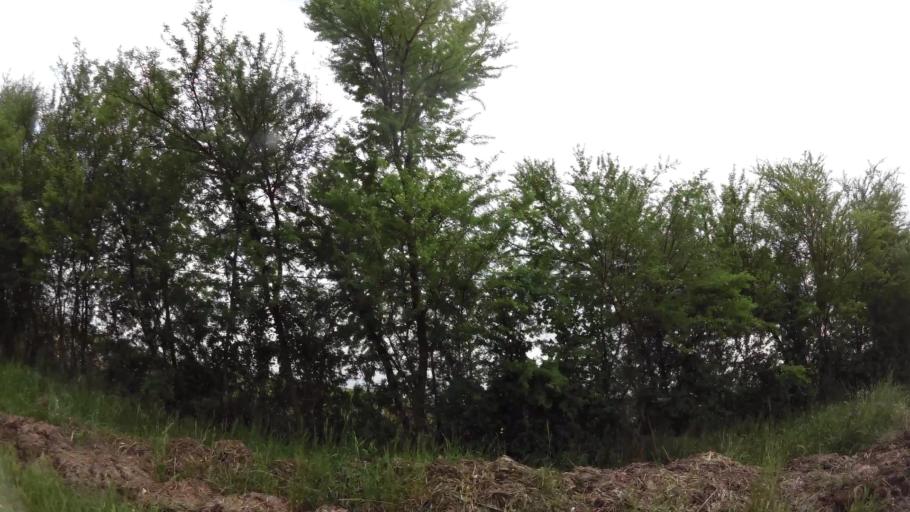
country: MA
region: Rabat-Sale-Zemmour-Zaer
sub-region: Khemisset
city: Tiflet
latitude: 33.7571
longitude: -6.2289
